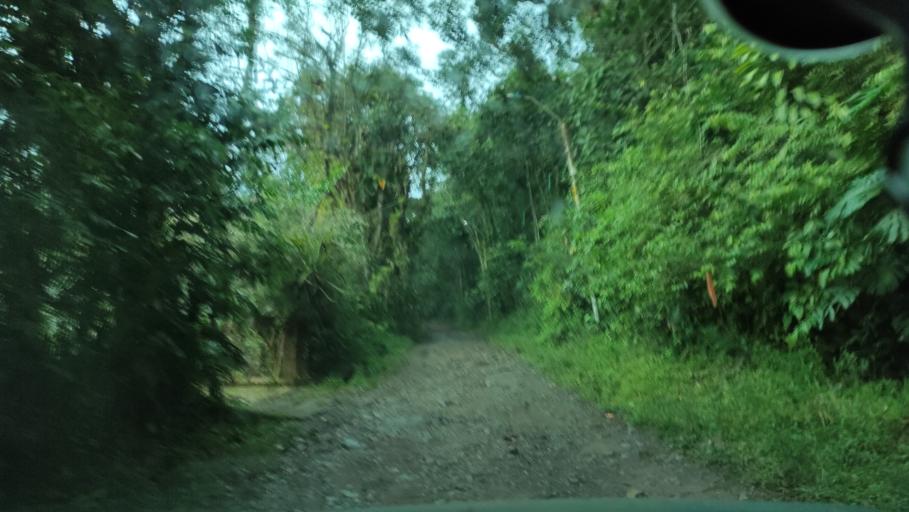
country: CO
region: Valle del Cauca
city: Jamundi
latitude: 3.3232
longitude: -76.6330
